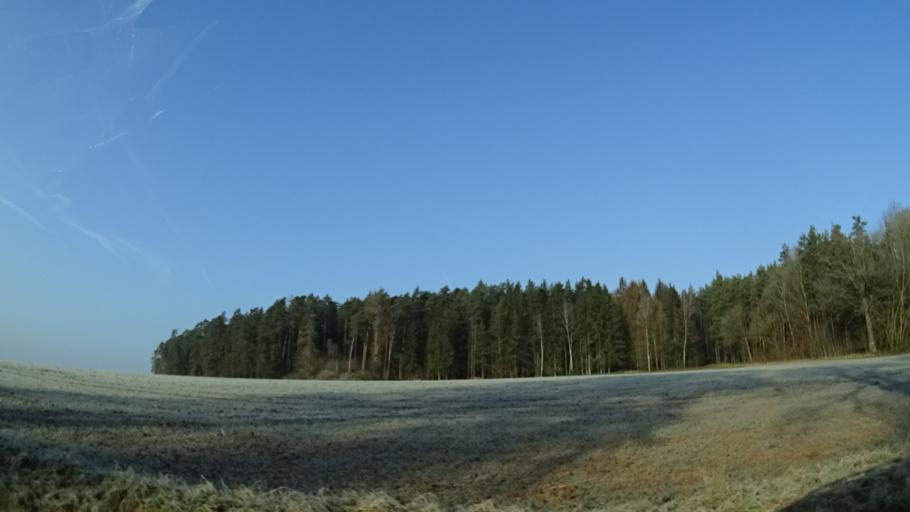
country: DE
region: Bavaria
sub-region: Upper Franconia
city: Weitramsdorf
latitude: 50.2449
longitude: 10.9046
